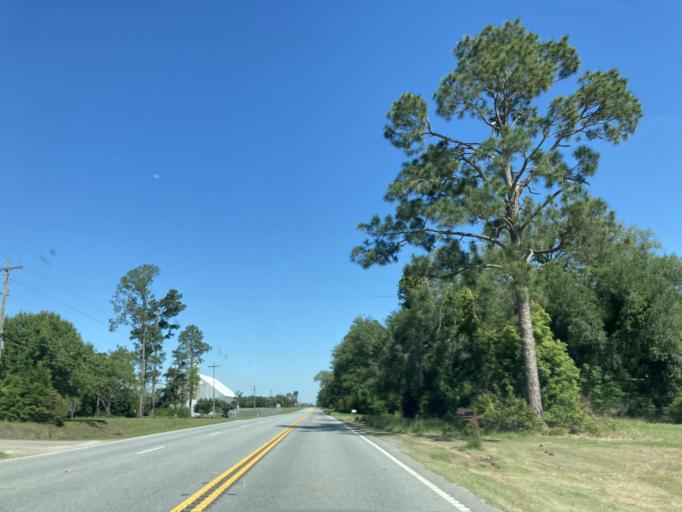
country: US
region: Georgia
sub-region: Miller County
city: Colquitt
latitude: 31.1854
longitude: -84.6064
